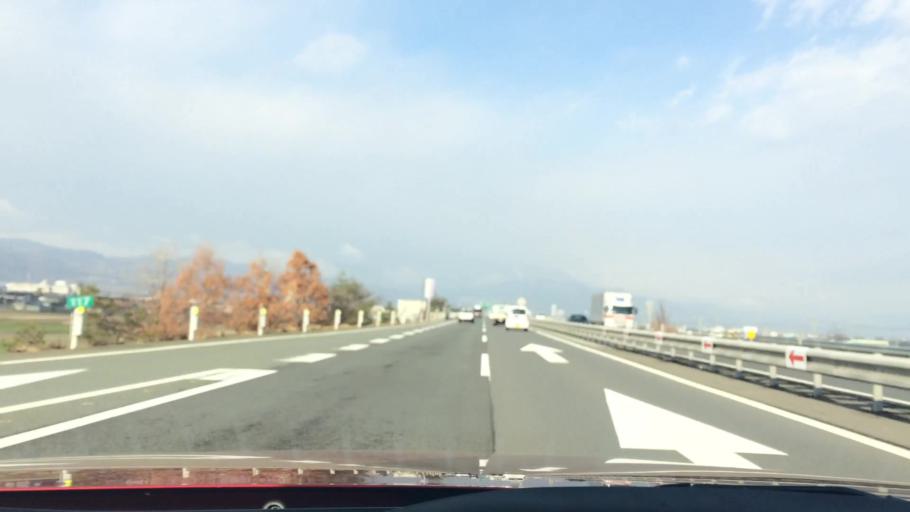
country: JP
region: Nagano
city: Nagano-shi
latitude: 36.5369
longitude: 138.1399
